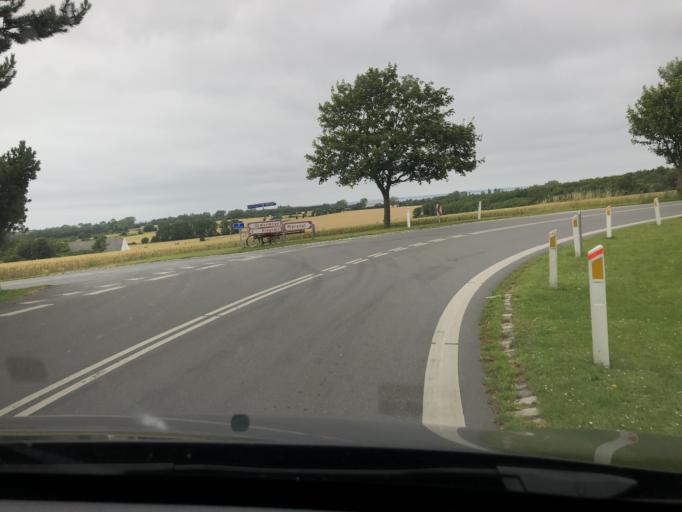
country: DK
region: South Denmark
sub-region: AEro Kommune
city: Marstal
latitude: 54.8548
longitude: 10.4980
